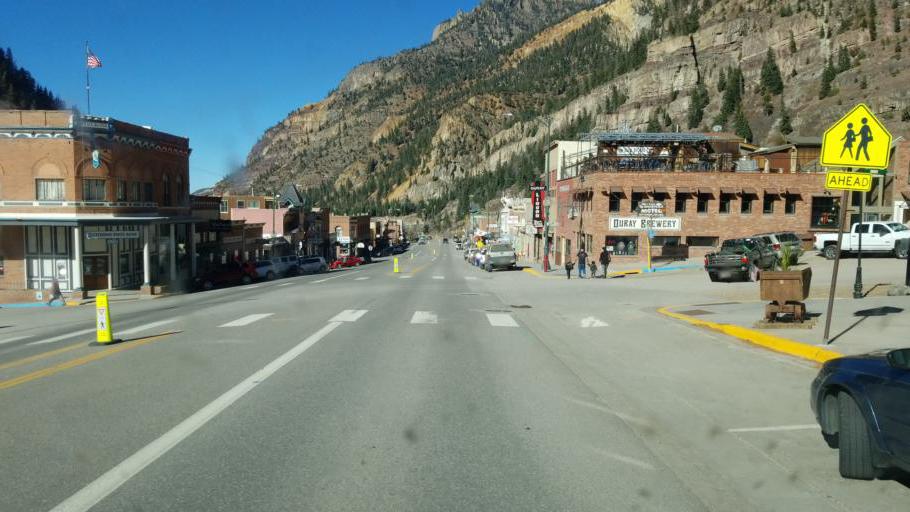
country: US
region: Colorado
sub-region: Ouray County
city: Ouray
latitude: 38.0225
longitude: -107.6714
